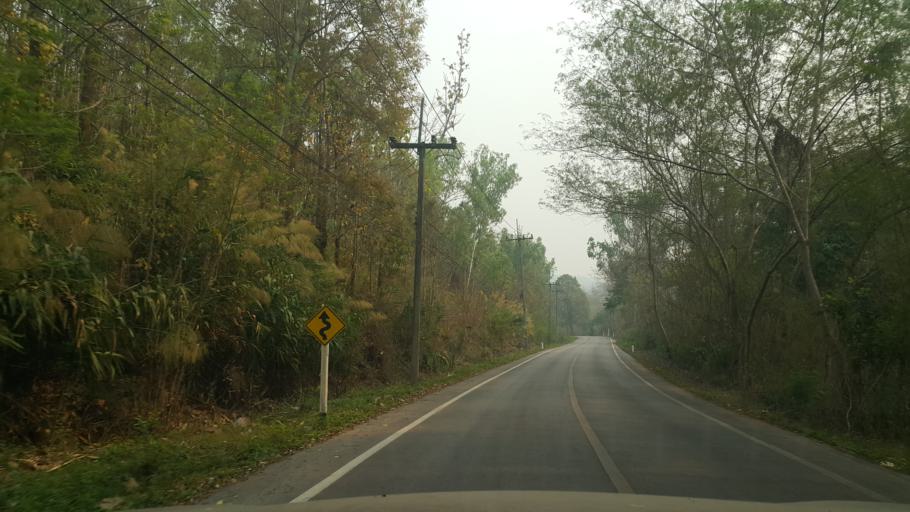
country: TH
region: Chiang Mai
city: Mae On
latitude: 18.7037
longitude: 99.3005
